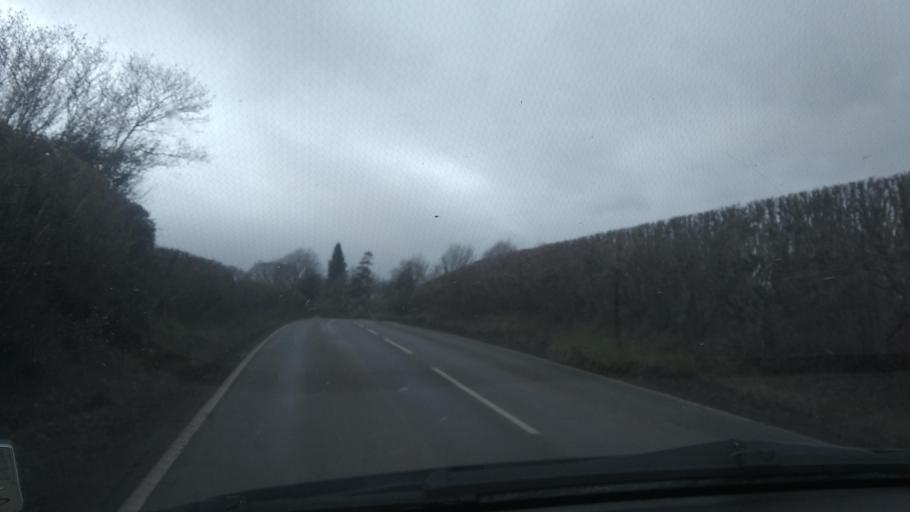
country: GB
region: England
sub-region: Shropshire
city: Cleobury Mortimer
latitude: 52.3741
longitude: -2.4168
